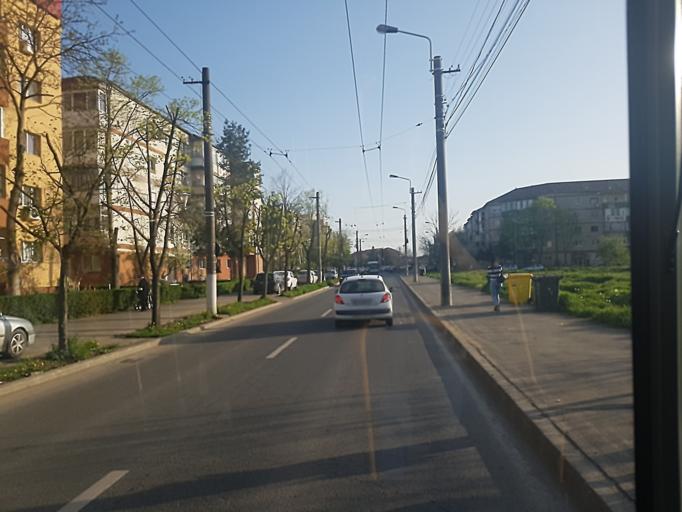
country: RO
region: Timis
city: Timisoara
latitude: 45.7336
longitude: 21.2483
